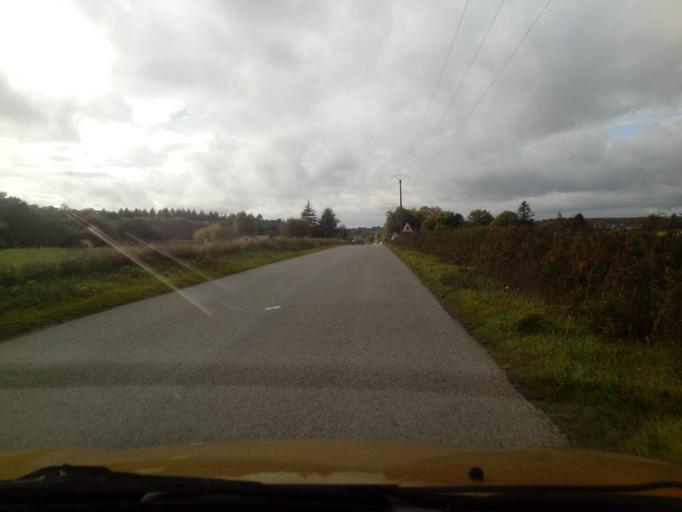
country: FR
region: Brittany
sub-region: Departement du Morbihan
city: Mauron
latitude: 48.0864
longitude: -2.3425
